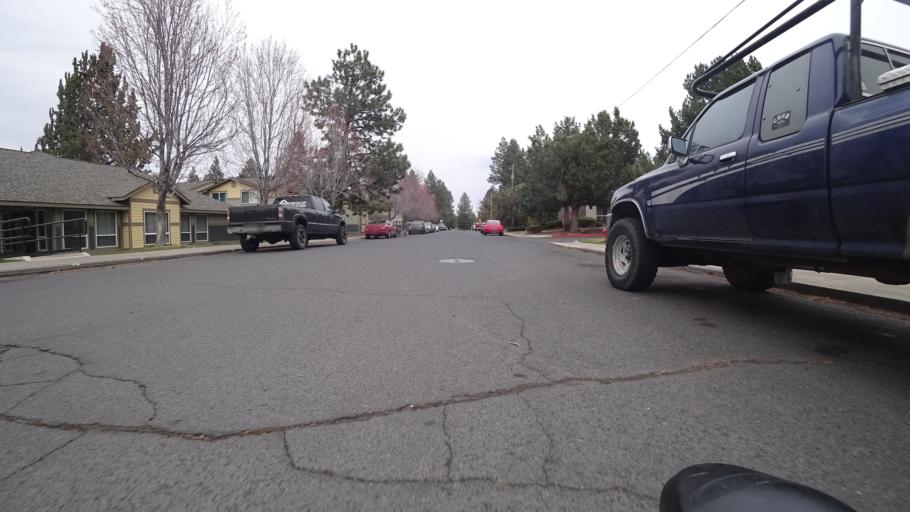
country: US
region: Oregon
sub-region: Deschutes County
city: Bend
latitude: 44.0460
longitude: -121.2805
